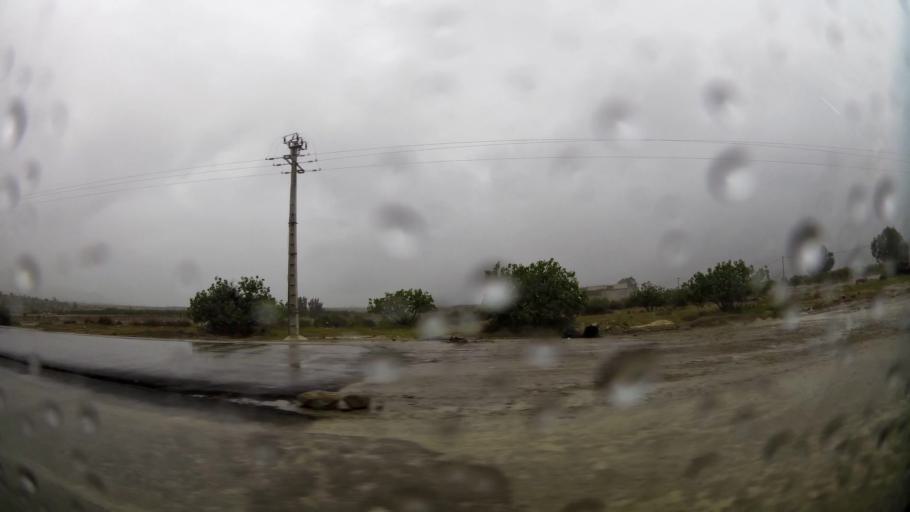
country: MA
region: Oriental
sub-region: Nador
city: Midar
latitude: 34.8775
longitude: -3.7260
